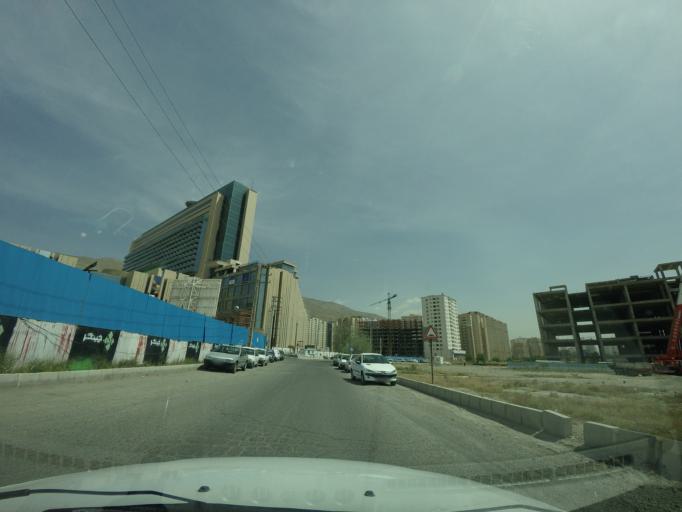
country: IR
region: Tehran
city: Shahr-e Qods
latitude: 35.7517
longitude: 51.1942
